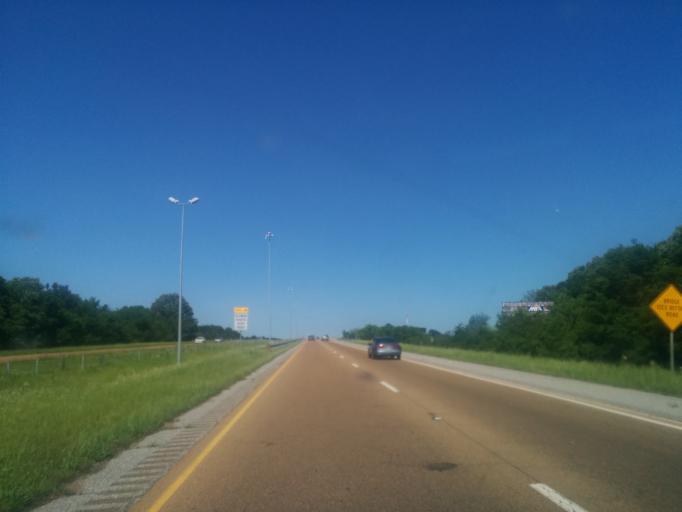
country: US
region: Mississippi
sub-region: Hinds County
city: Jackson
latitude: 32.3668
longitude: -90.2250
